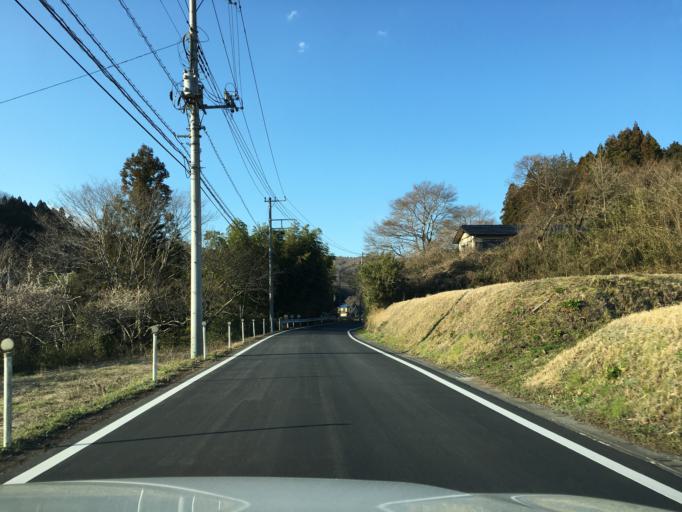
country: JP
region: Tochigi
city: Karasuyama
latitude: 36.7594
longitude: 140.2021
